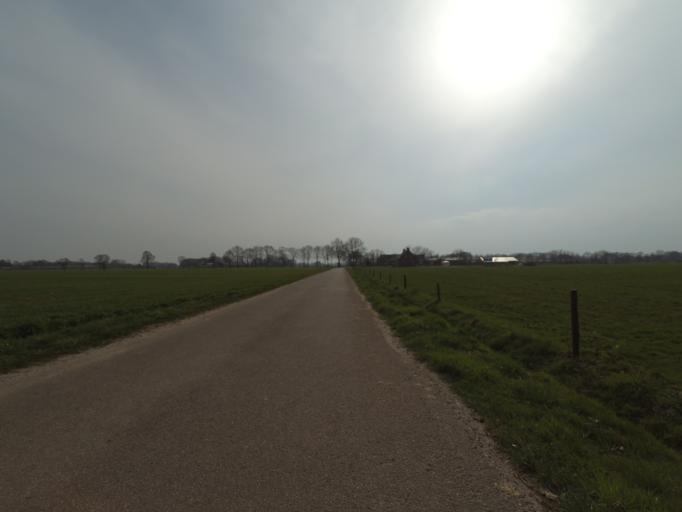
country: NL
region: Gelderland
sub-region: Gemeente Ede
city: Ederveen
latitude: 52.0942
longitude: 5.5894
